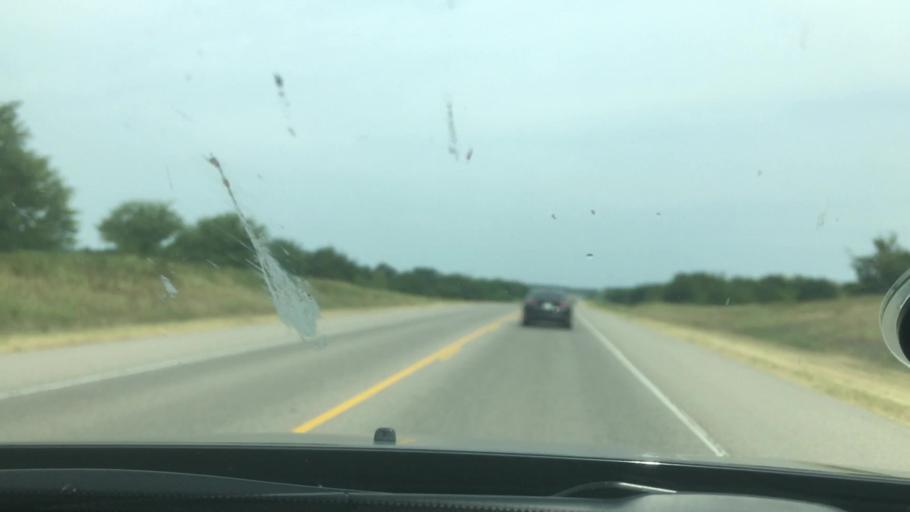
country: US
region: Oklahoma
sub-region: Pontotoc County
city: Ada
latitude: 34.7132
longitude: -96.6200
